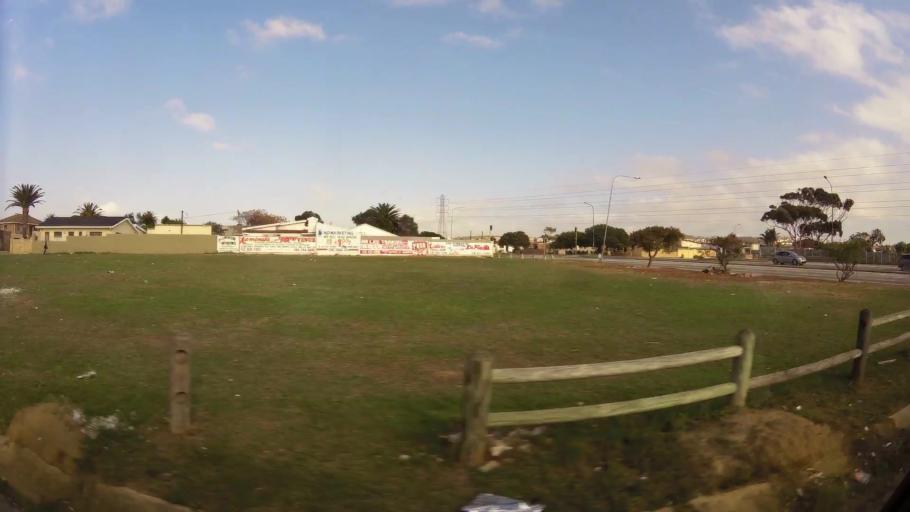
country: ZA
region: Eastern Cape
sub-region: Nelson Mandela Bay Metropolitan Municipality
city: Port Elizabeth
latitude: -33.9165
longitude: 25.5606
